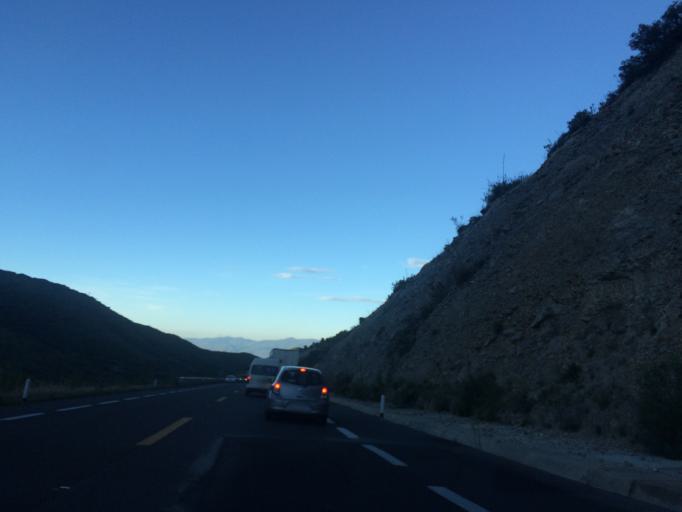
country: MX
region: Puebla
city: Chapuco
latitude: 18.6415
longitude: -97.4579
